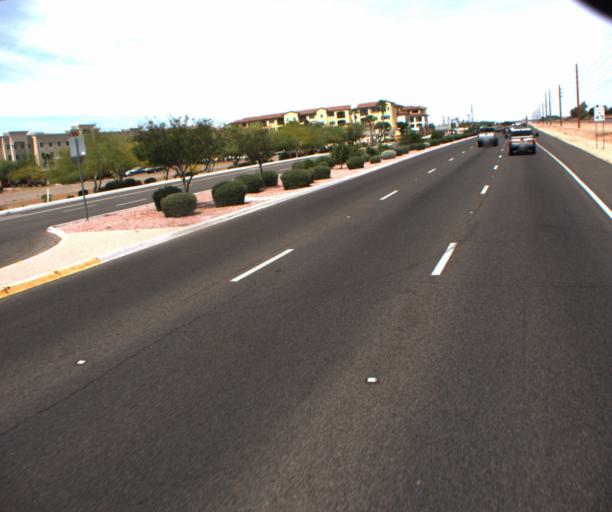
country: US
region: Arizona
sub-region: Maricopa County
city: Sun City West
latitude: 33.6581
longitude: -112.3750
